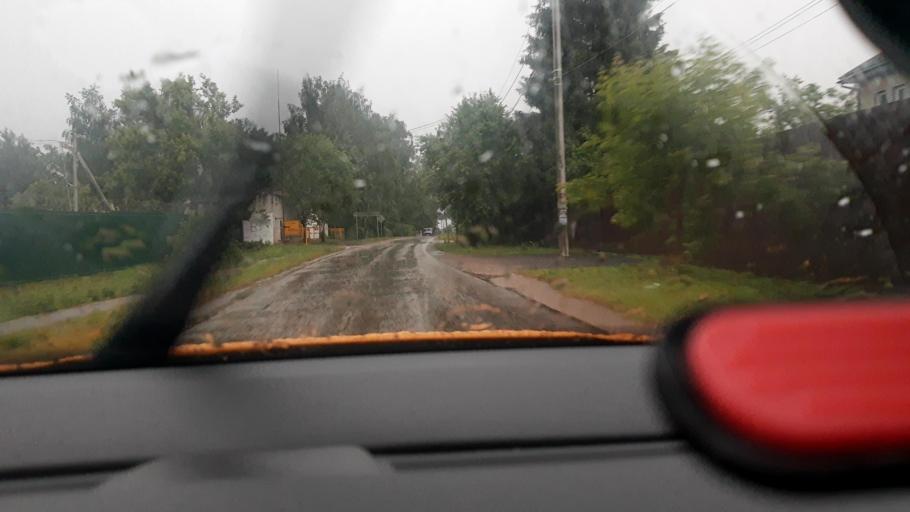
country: RU
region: Moskovskaya
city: Alabushevo
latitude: 56.0054
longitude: 37.1375
